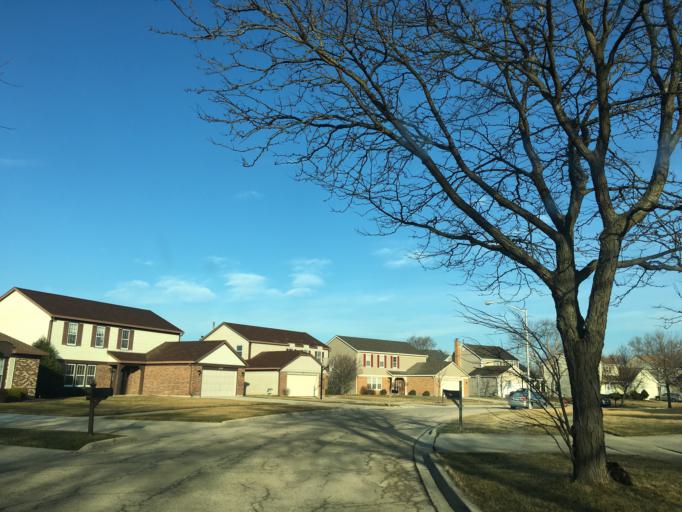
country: US
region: Illinois
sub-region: Cook County
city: Schaumburg
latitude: 42.0464
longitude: -88.1149
